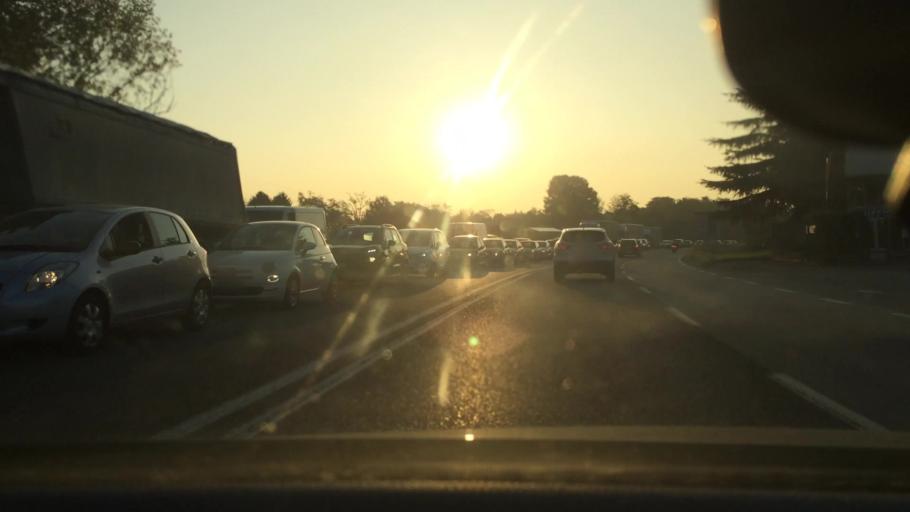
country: IT
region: Lombardy
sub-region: Citta metropolitana di Milano
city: Passirana
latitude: 45.5389
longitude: 9.0444
